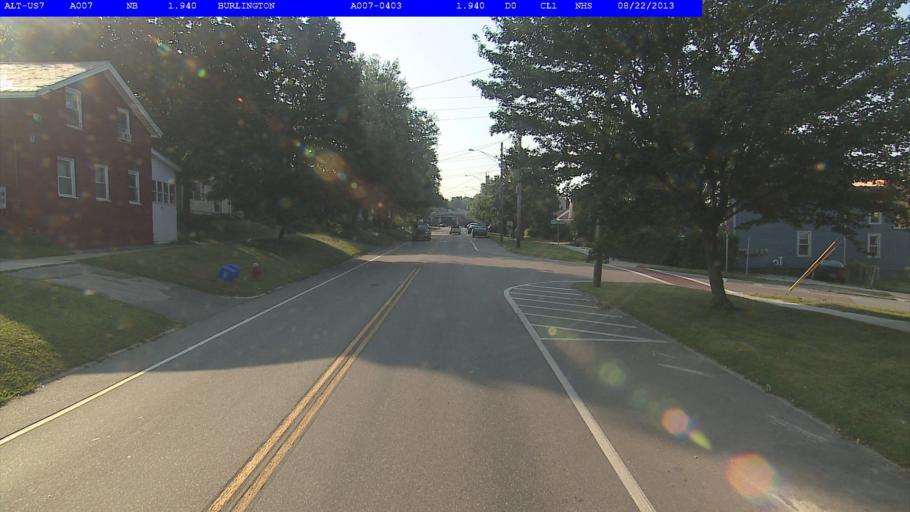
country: US
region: Vermont
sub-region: Chittenden County
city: Burlington
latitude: 44.4666
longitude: -73.2091
